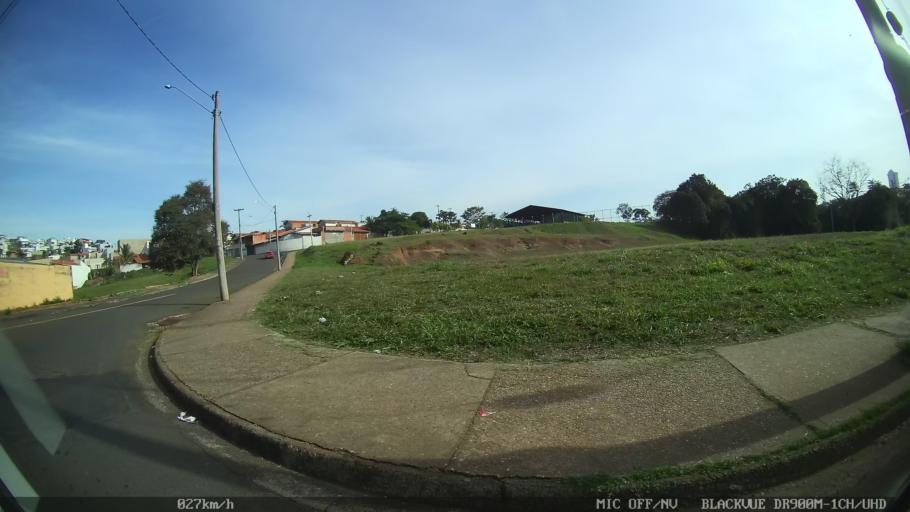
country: BR
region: Sao Paulo
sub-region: Piracicaba
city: Piracicaba
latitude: -22.7372
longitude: -47.6684
